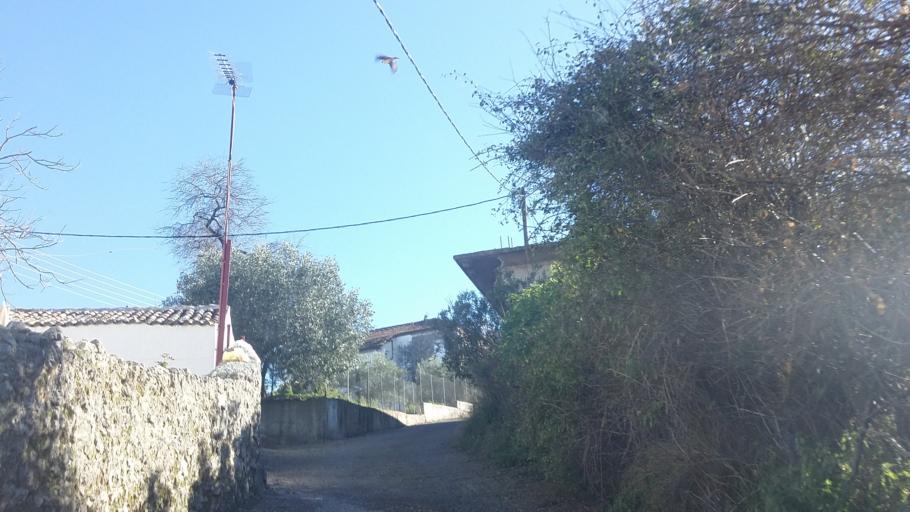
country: GR
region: West Greece
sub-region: Nomos Aitolias kai Akarnanias
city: Fitiai
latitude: 38.7114
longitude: 21.1732
